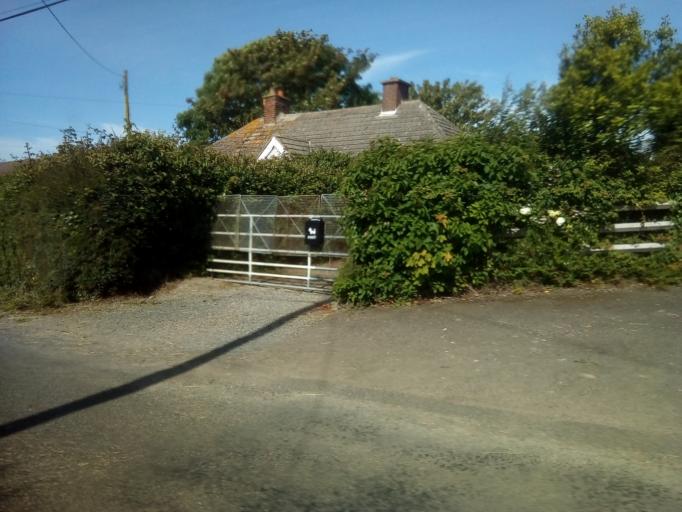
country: IE
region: Leinster
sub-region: Loch Garman
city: Loch Garman
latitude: 52.2115
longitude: -6.5418
